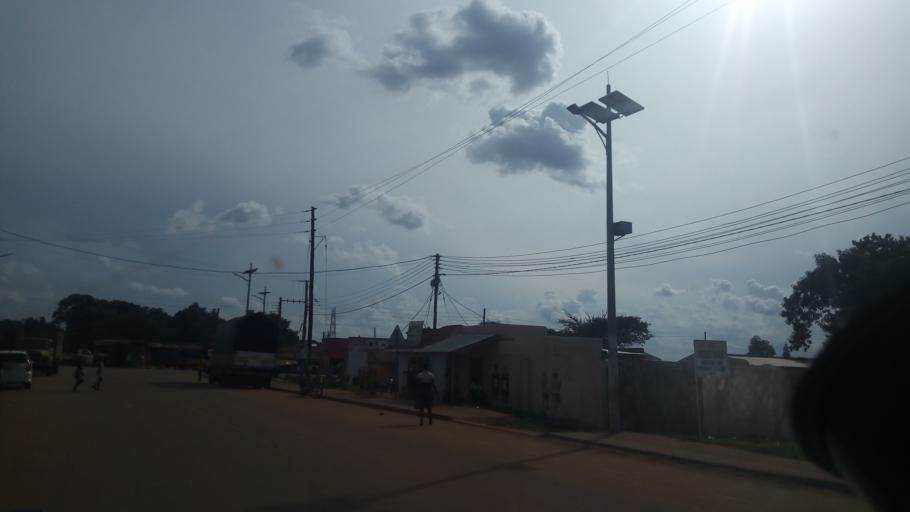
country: UG
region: Northern Region
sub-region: Lira District
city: Lira
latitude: 2.2395
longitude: 32.8904
